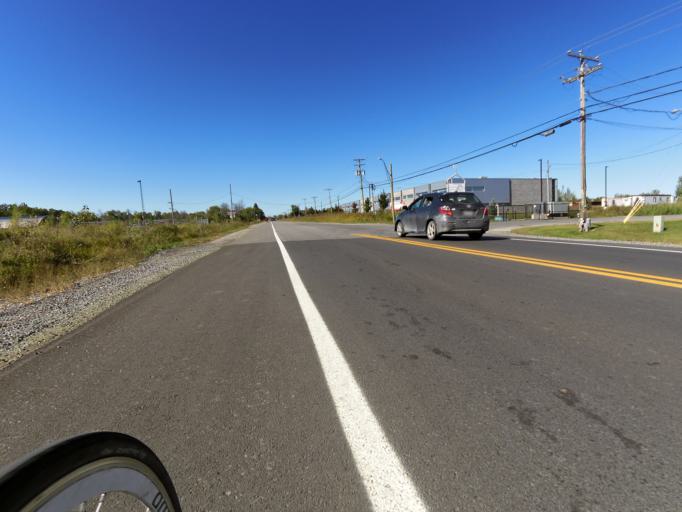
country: CA
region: Quebec
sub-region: Outaouais
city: Gatineau
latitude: 45.5063
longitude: -75.5489
